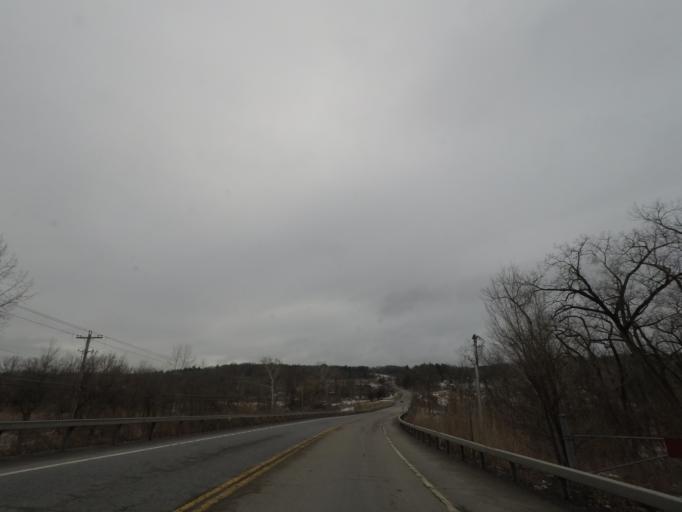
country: US
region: New York
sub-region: Albany County
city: Voorheesville
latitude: 42.6799
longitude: -73.9052
